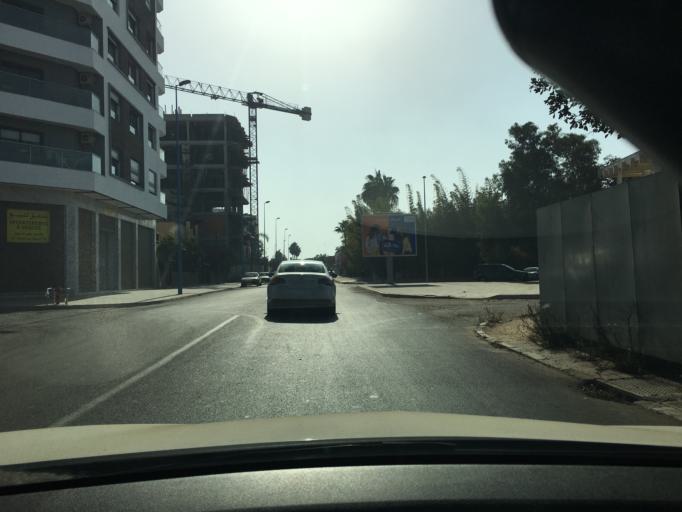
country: MA
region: Grand Casablanca
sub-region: Casablanca
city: Casablanca
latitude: 33.5803
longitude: -7.6485
